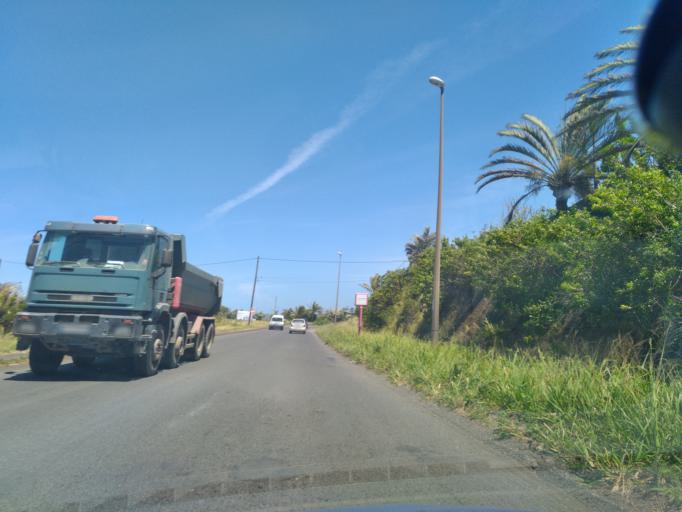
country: RE
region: Reunion
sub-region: Reunion
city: Saint-Pierre
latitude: -21.3264
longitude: 55.4502
